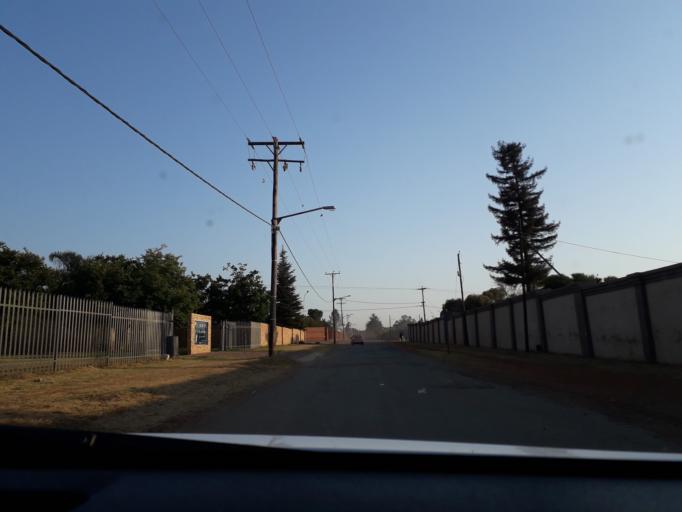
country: ZA
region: Gauteng
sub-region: Ekurhuleni Metropolitan Municipality
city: Benoni
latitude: -26.1109
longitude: 28.3018
